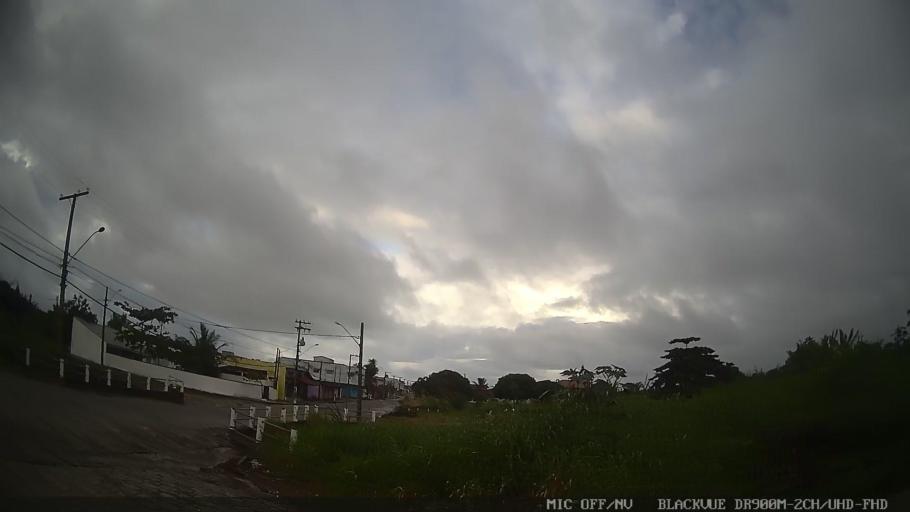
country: BR
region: Sao Paulo
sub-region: Itanhaem
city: Itanhaem
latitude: -24.2109
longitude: -46.8544
